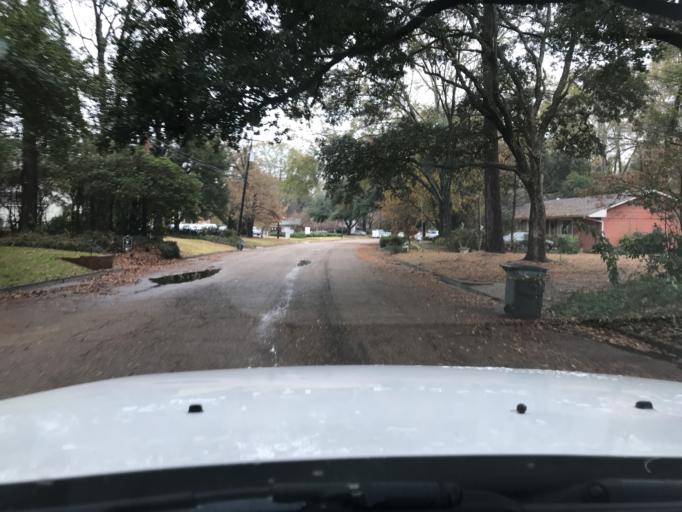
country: US
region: Mississippi
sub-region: Rankin County
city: Flowood
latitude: 32.3459
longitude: -90.1678
